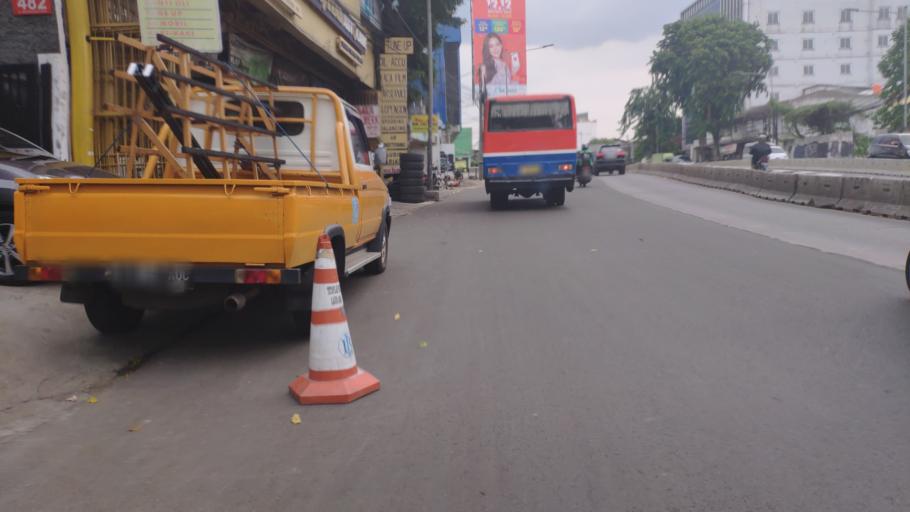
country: ID
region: Jakarta Raya
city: Jakarta
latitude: -6.2730
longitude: 106.8303
